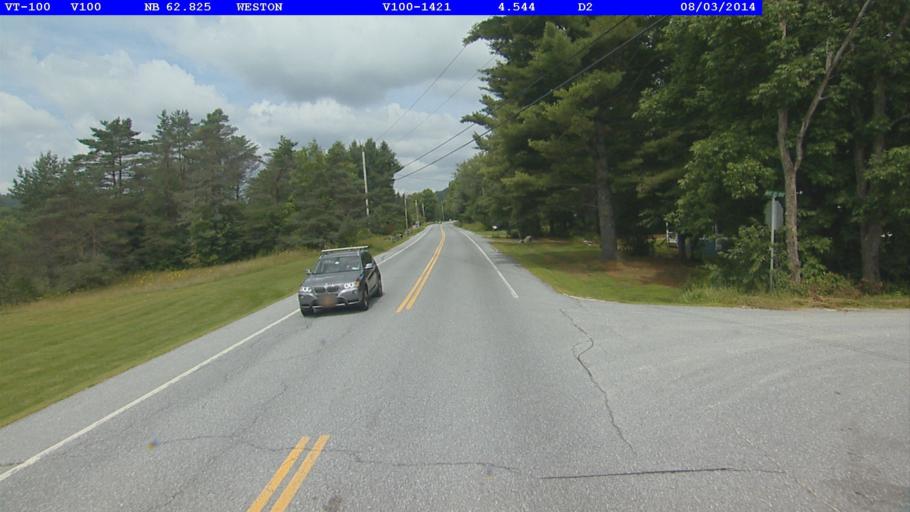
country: US
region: Vermont
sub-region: Windsor County
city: Chester
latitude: 43.3097
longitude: -72.7869
